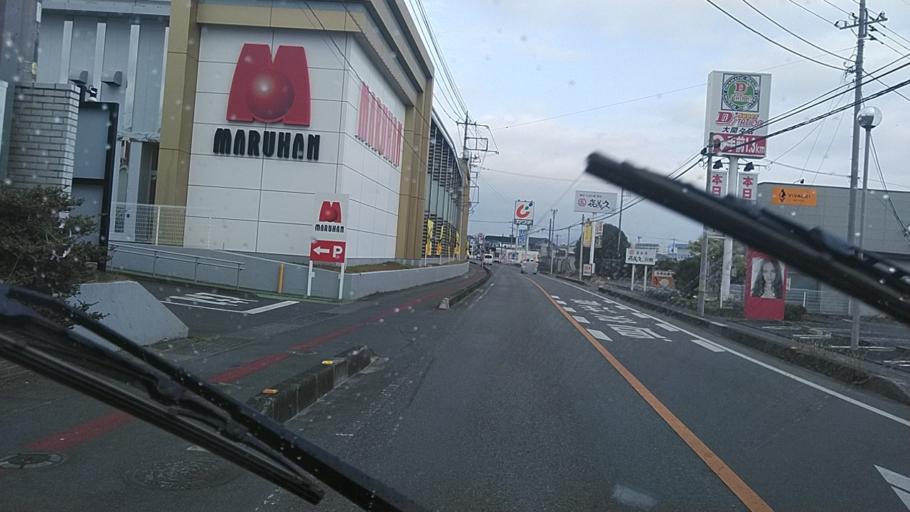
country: JP
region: Gunma
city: Omamacho-omama
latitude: 36.4158
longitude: 139.2875
